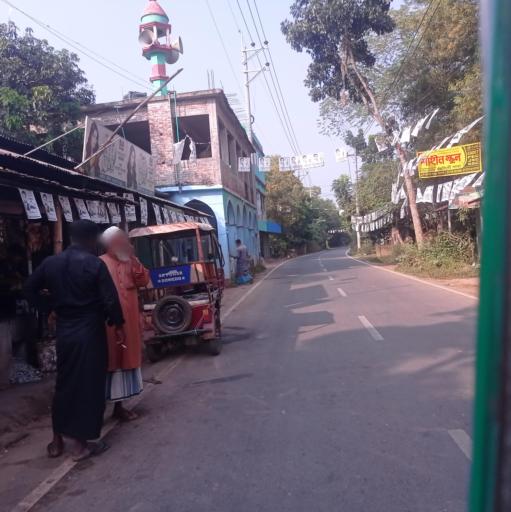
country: BD
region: Dhaka
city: Bhairab Bazar
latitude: 24.0458
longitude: 90.8347
